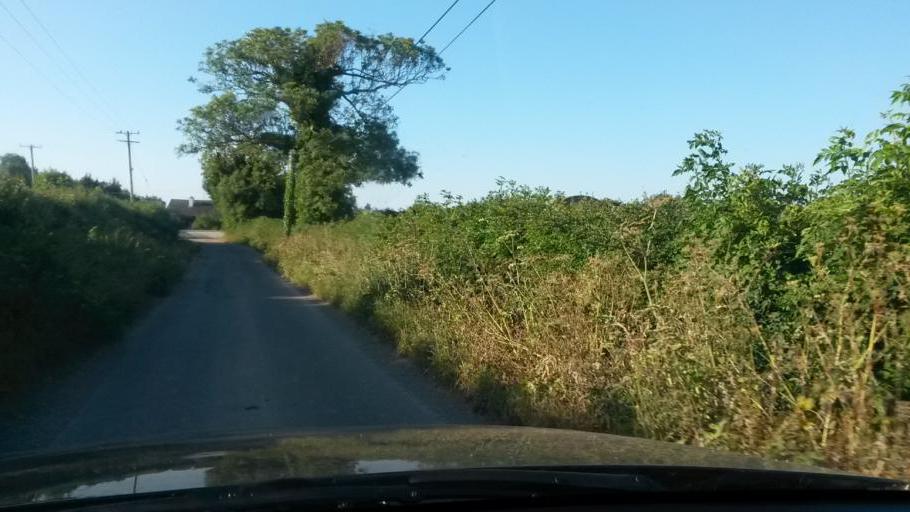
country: IE
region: Leinster
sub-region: Fingal County
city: Swords
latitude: 53.4943
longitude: -6.2833
